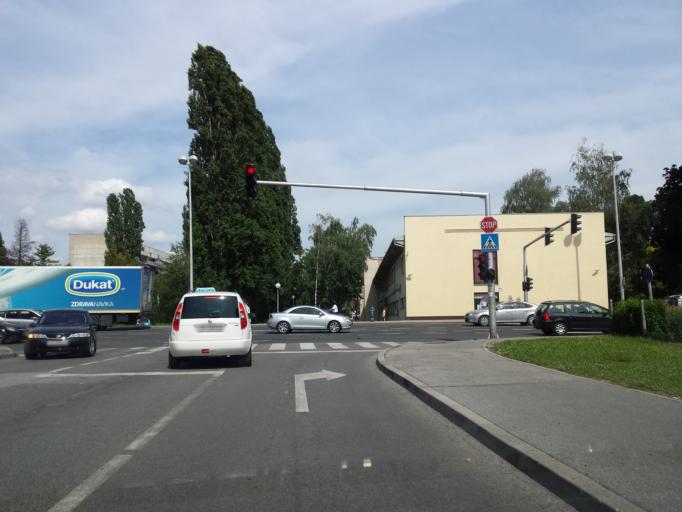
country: HR
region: Grad Zagreb
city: Zagreb - Centar
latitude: 45.8013
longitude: 15.9430
